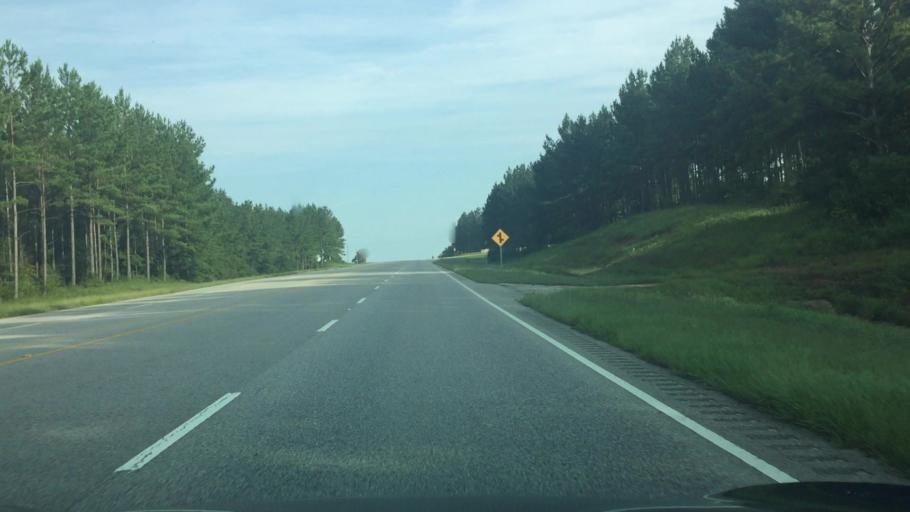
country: US
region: Alabama
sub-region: Butler County
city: Georgiana
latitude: 31.4803
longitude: -86.6755
